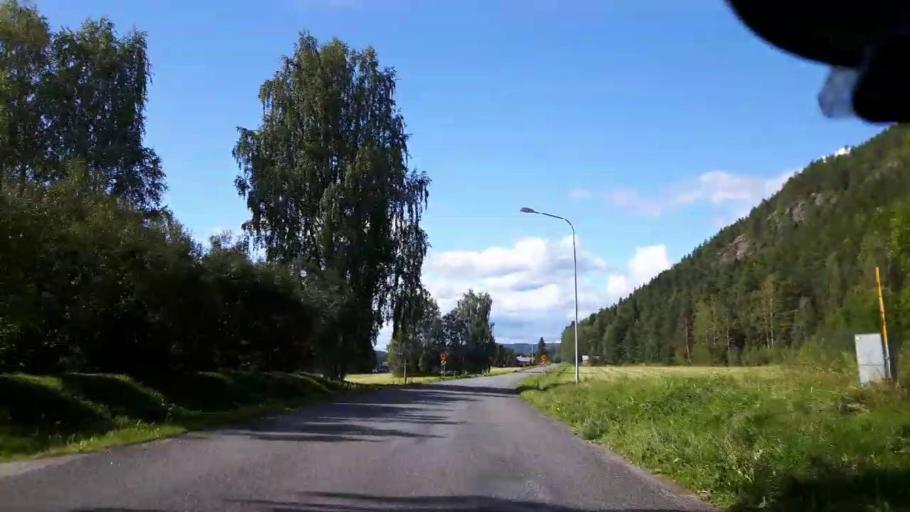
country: SE
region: Jaemtland
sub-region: Braecke Kommun
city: Braecke
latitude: 63.1697
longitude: 15.5763
